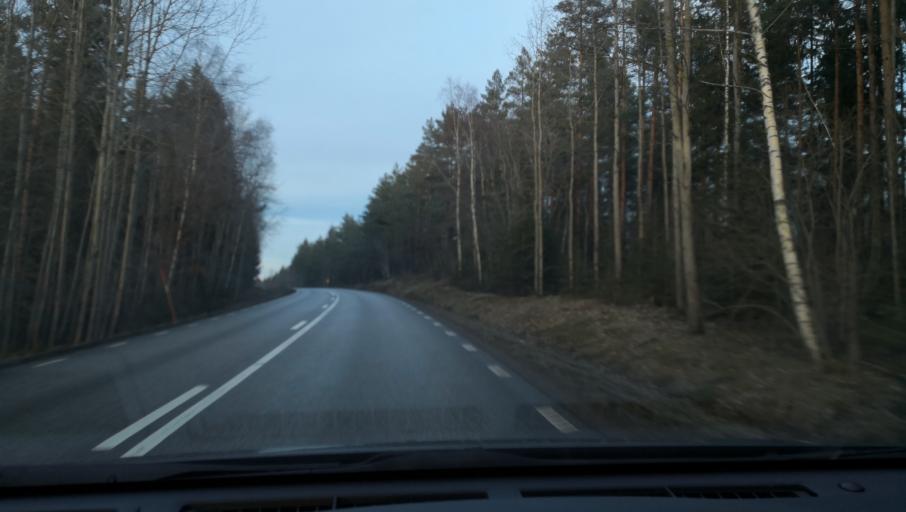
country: SE
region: OErebro
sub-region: Laxa Kommun
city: Laxa
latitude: 59.1422
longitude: 14.6815
